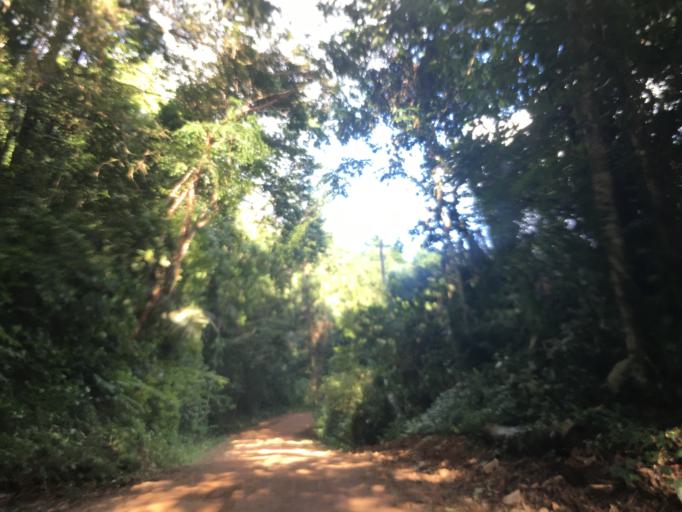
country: BZ
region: Stann Creek
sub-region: Dangriga
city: Dangriga
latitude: 16.7942
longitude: -88.4276
